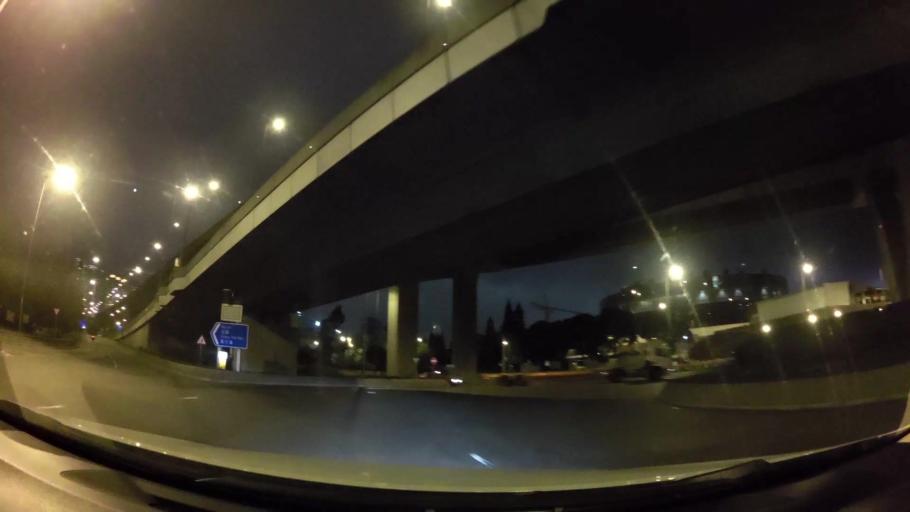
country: HK
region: Sham Shui Po
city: Sham Shui Po
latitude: 22.3272
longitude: 114.1377
